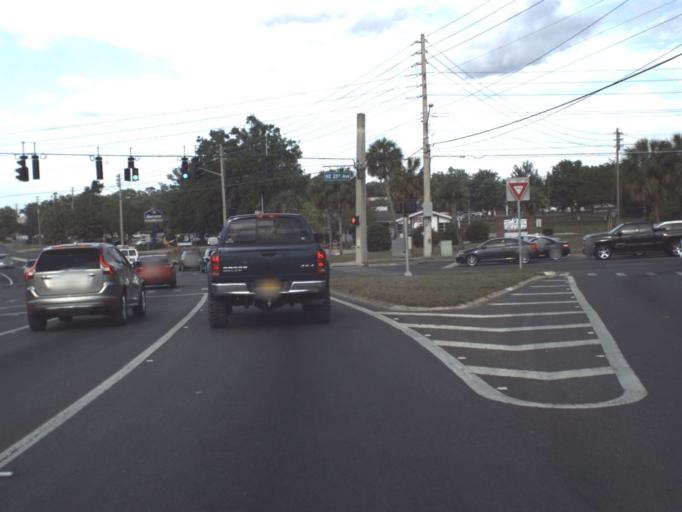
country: US
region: Florida
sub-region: Marion County
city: Ocala
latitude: 29.1868
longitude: -82.1037
